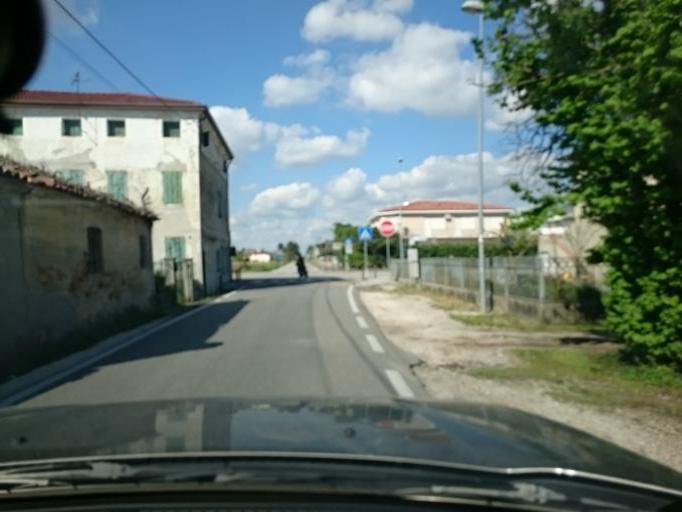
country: IT
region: Veneto
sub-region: Provincia di Padova
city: Villanova
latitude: 45.4870
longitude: 11.9858
